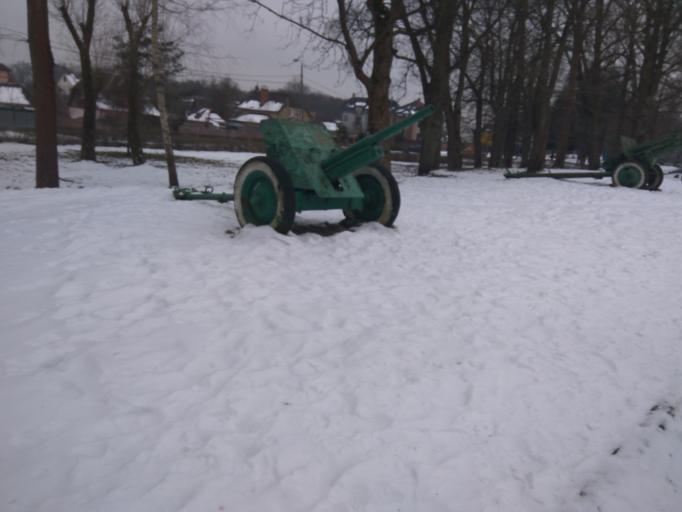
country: RU
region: Kaliningrad
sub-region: Gorod Kaliningrad
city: Kaliningrad
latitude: 54.7525
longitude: 20.4453
